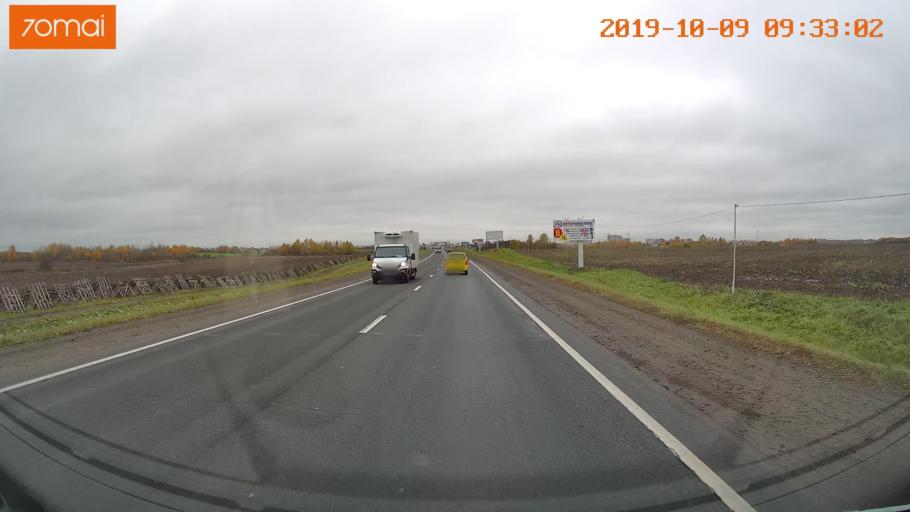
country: RU
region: Vologda
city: Vologda
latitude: 59.1646
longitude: 39.9207
